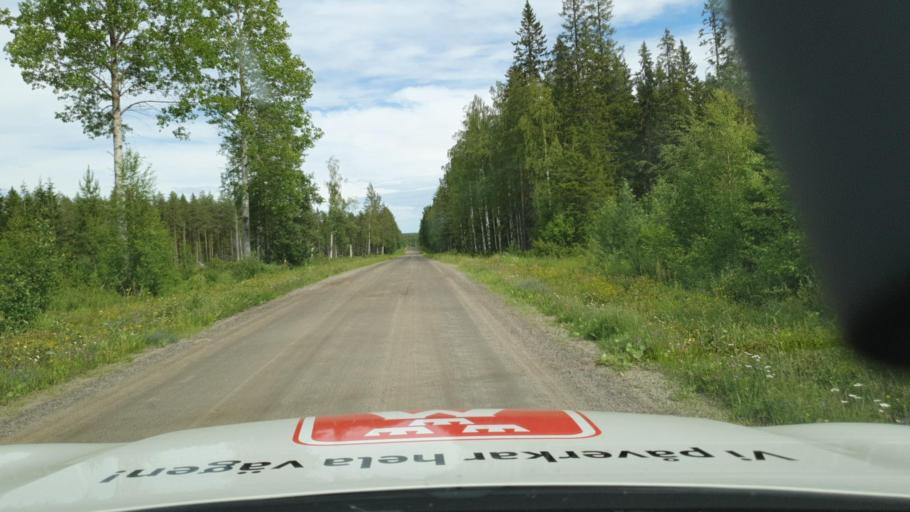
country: SE
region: Vaesterbotten
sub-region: Skelleftea Kommun
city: Burtraesk
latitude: 64.4900
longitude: 20.5676
